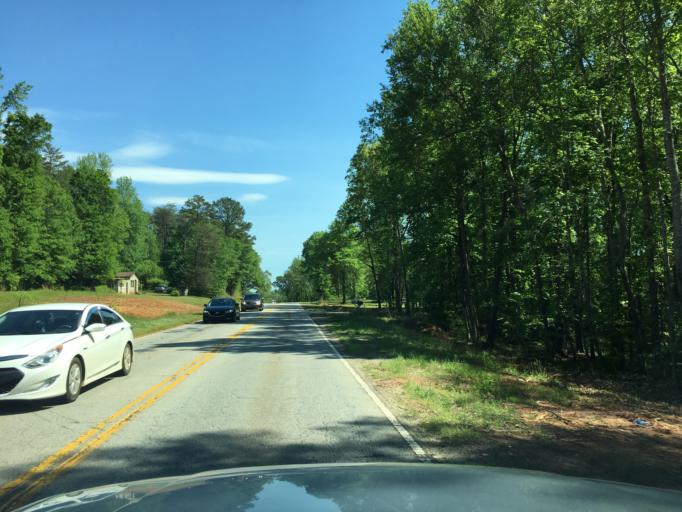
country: US
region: South Carolina
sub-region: Spartanburg County
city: Wellford
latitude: 34.9645
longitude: -82.0855
